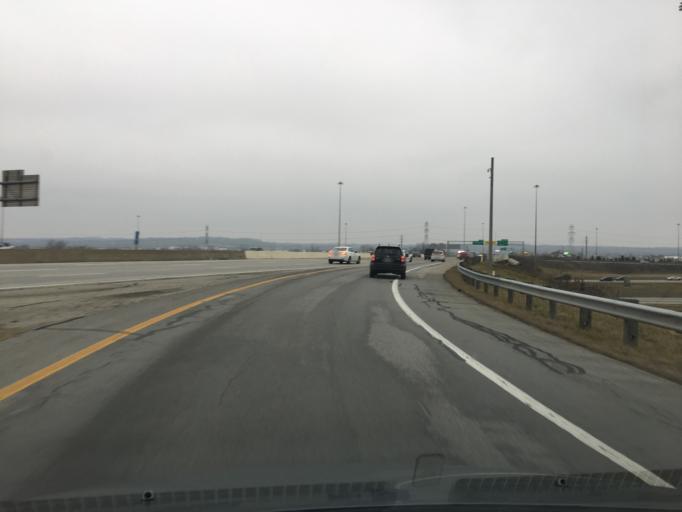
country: US
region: Ohio
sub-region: Hamilton County
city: Glendale
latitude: 39.2905
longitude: -84.4437
